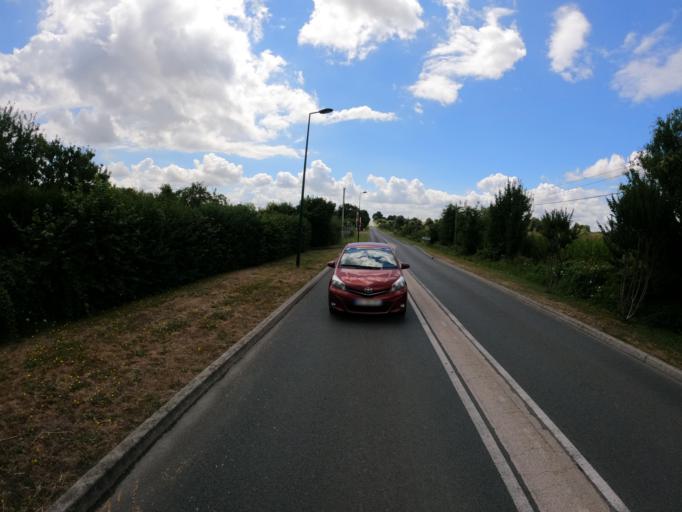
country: FR
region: Pays de la Loire
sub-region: Departement de Maine-et-Loire
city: Mire
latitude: 47.7271
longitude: -0.5195
